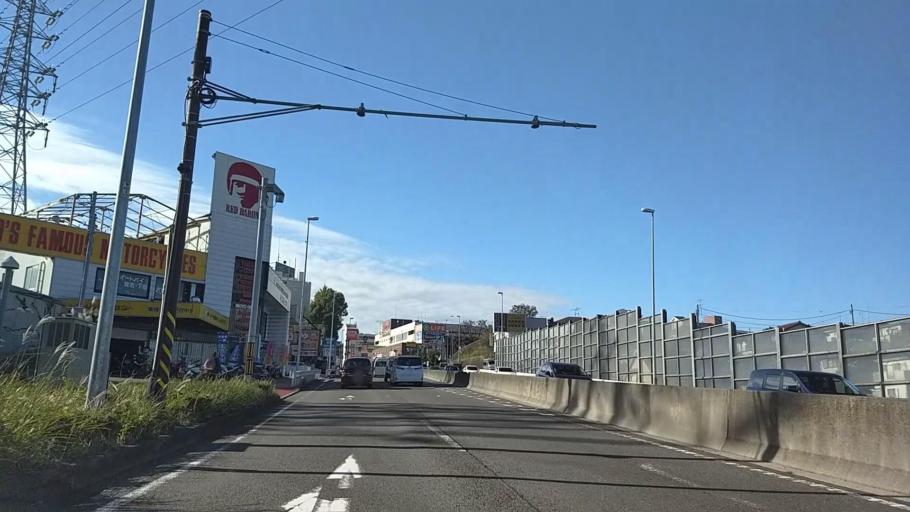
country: JP
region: Kanagawa
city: Fujisawa
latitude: 35.3919
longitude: 139.5230
